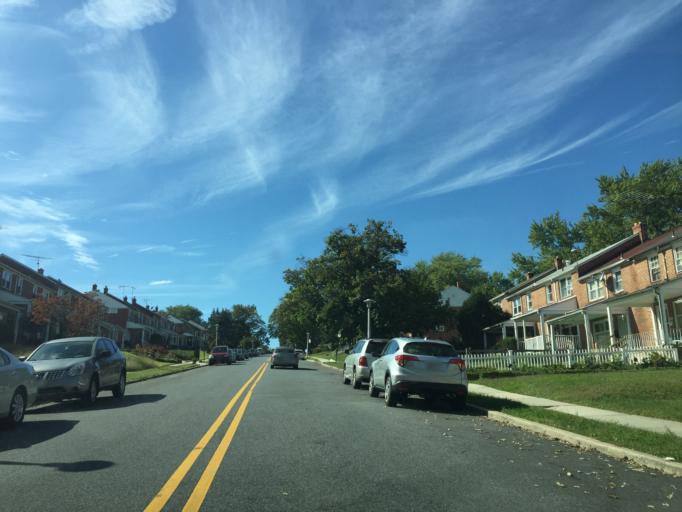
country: US
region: Maryland
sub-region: Baltimore County
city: Towson
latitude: 39.3704
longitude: -76.5841
